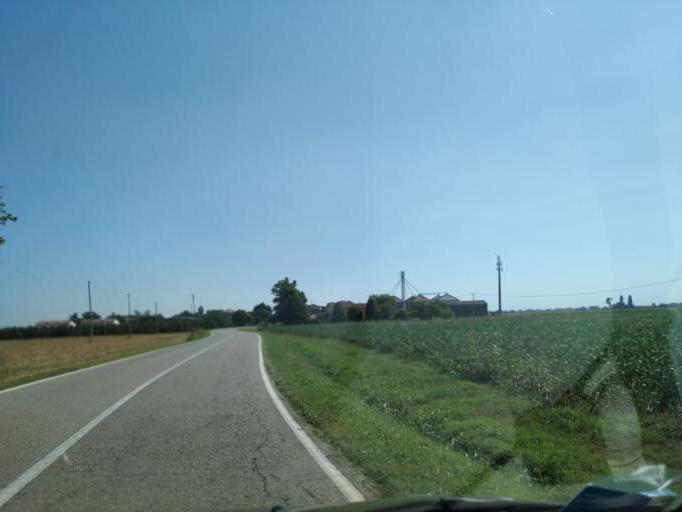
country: IT
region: Emilia-Romagna
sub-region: Provincia di Ferrara
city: Coccanile-Cesta
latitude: 44.9120
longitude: 11.8993
